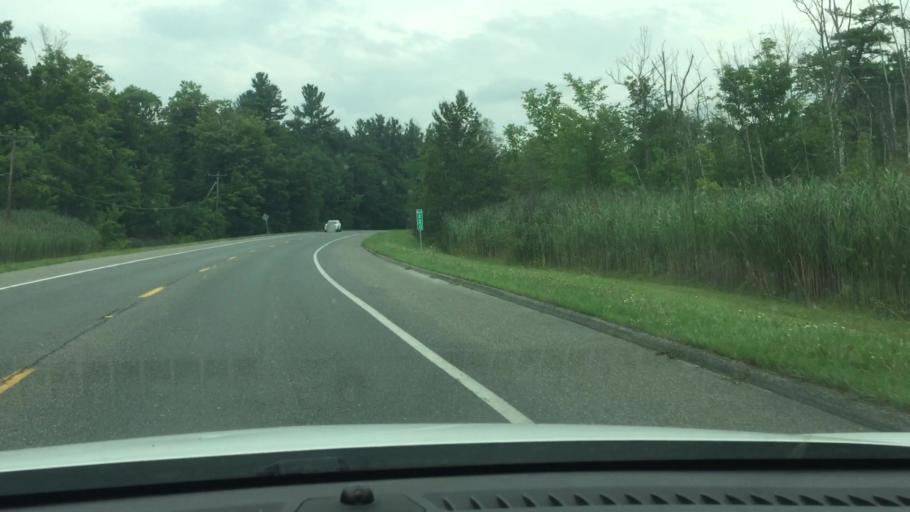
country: US
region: Massachusetts
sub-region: Berkshire County
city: Lenox
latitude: 42.3282
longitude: -73.2880
